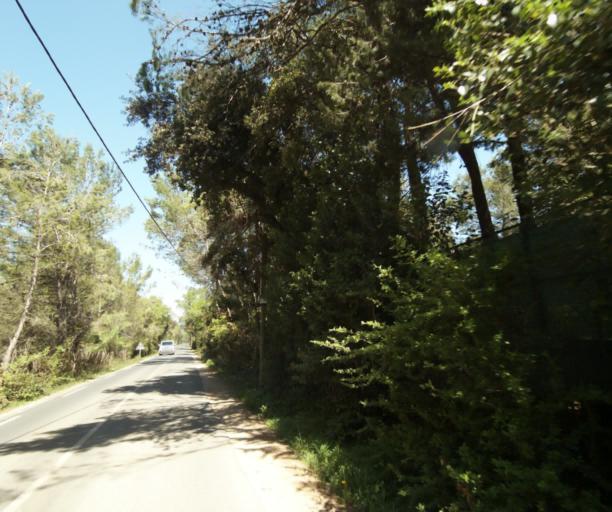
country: FR
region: Languedoc-Roussillon
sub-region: Departement de l'Herault
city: Saint-Genies-des-Mourgues
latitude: 43.6907
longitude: 4.0154
